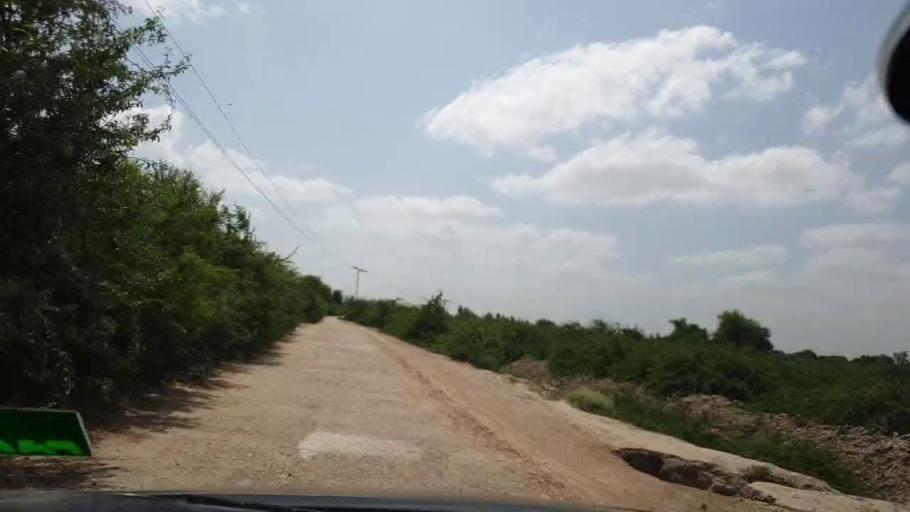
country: PK
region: Sindh
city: Kadhan
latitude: 24.5529
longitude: 69.2113
